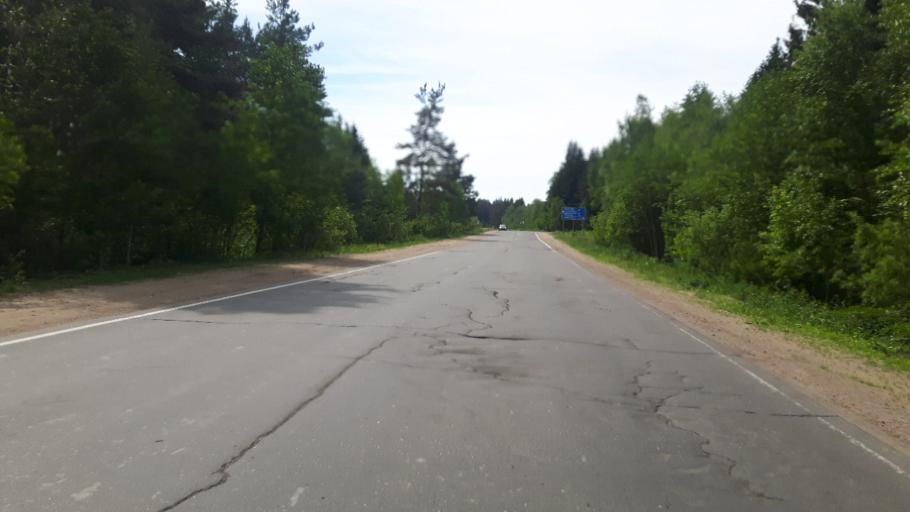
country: RU
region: Leningrad
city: Ust'-Luga
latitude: 59.6387
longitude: 28.2880
